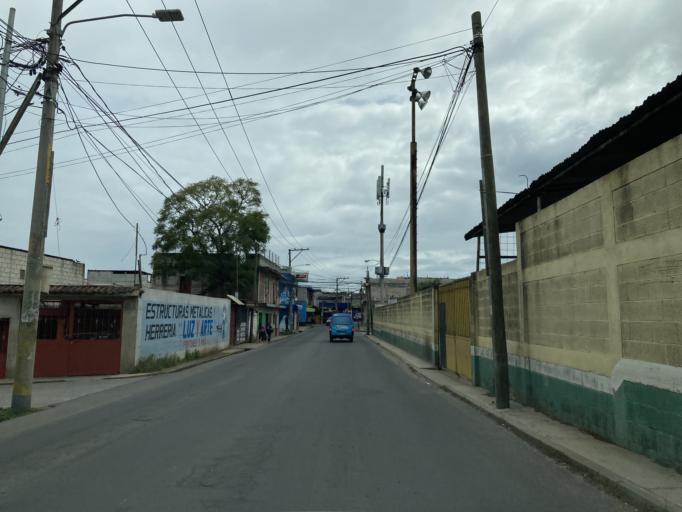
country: GT
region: Guatemala
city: San Jose Pinula
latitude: 14.5403
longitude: -90.4065
